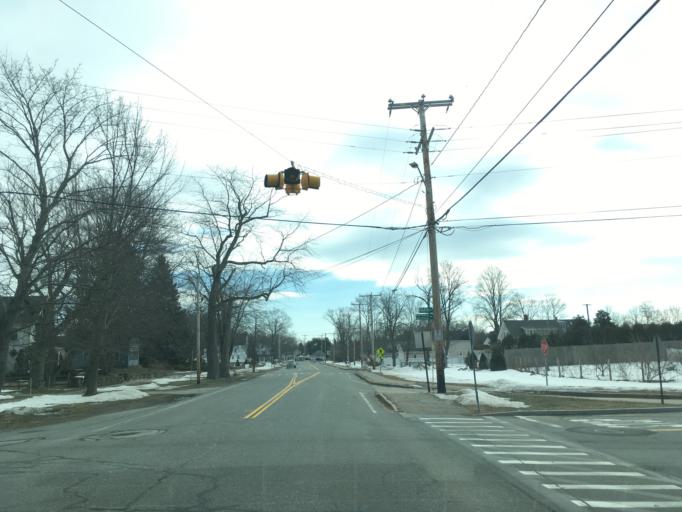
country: US
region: New Hampshire
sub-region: Rockingham County
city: Hampton
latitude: 42.9341
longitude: -70.8287
